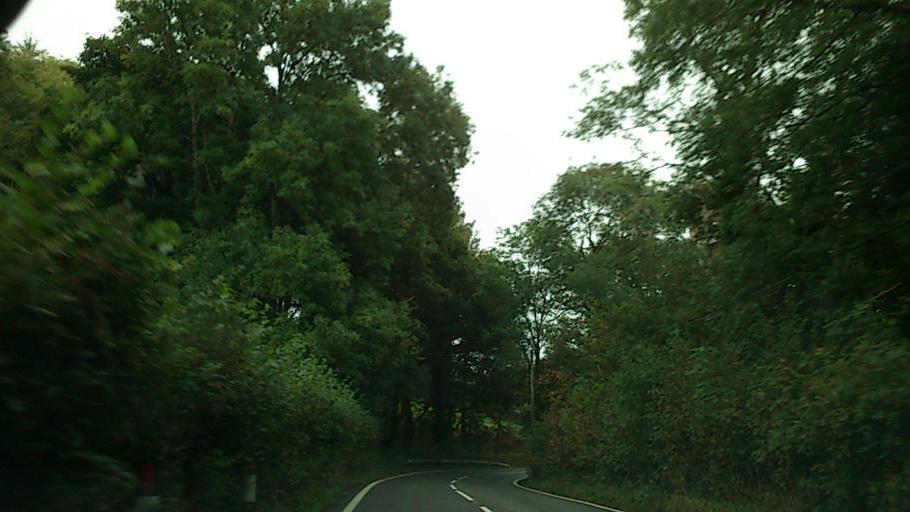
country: GB
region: Wales
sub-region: Gwynedd
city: Corris
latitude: 52.6998
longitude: -3.6572
